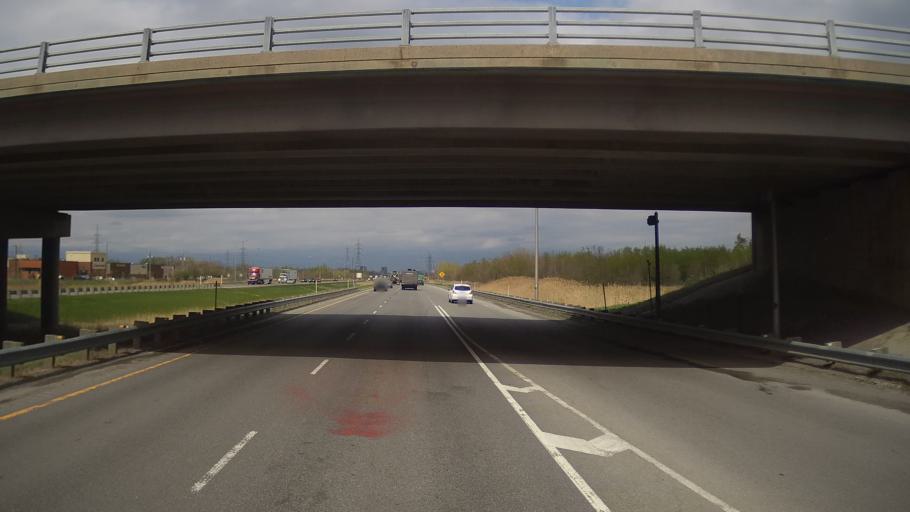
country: CA
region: Quebec
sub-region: Monteregie
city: La Prairie
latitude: 45.4033
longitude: -73.4611
